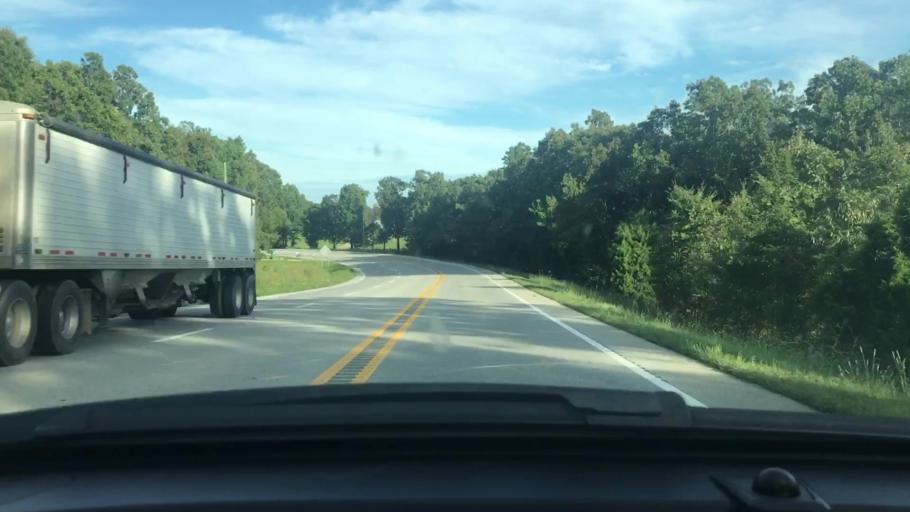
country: US
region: Arkansas
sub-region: Sharp County
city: Cherokee Village
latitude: 36.2723
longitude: -91.3713
